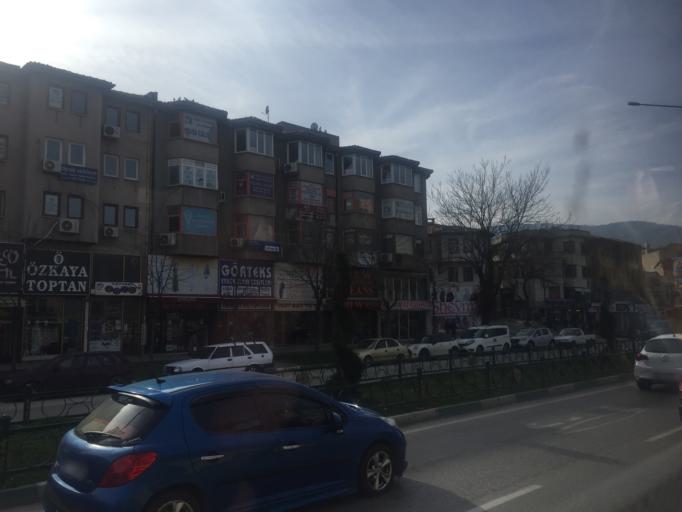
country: TR
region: Bursa
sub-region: Osmangazi
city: Bursa
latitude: 40.1879
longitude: 29.0659
